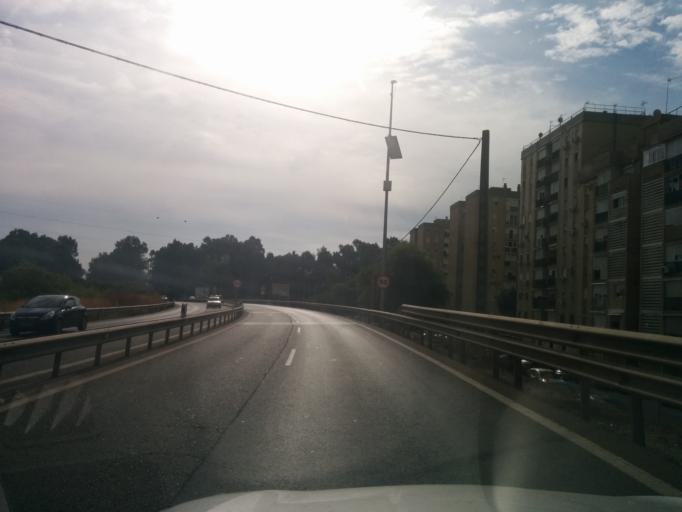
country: ES
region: Andalusia
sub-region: Provincia de Sevilla
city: Sevilla
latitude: 37.4246
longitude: -5.9605
